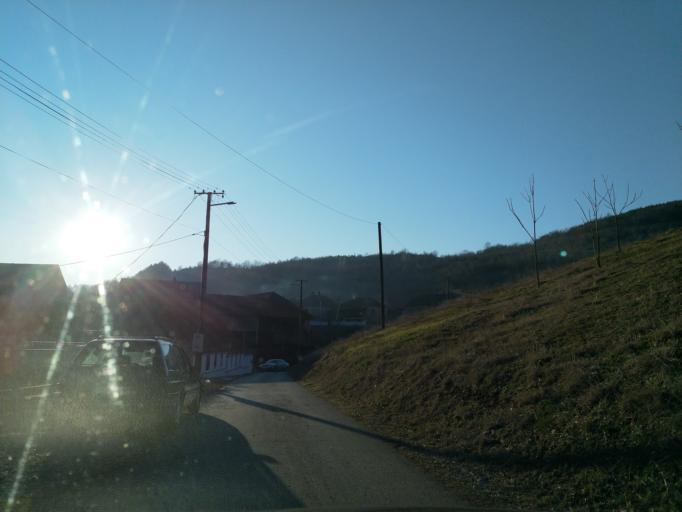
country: RS
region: Central Serbia
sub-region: Pomoravski Okrug
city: Paracin
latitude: 43.9366
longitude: 21.5236
